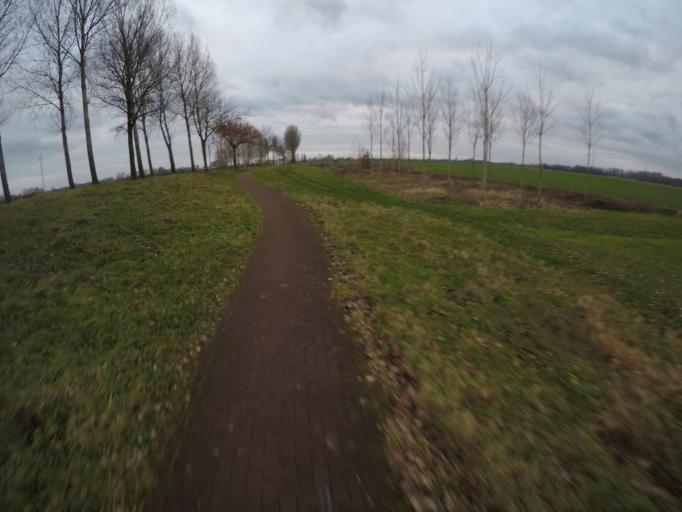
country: BE
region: Flanders
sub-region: Provincie Oost-Vlaanderen
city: Sint-Gillis-Waas
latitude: 51.2388
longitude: 4.1464
